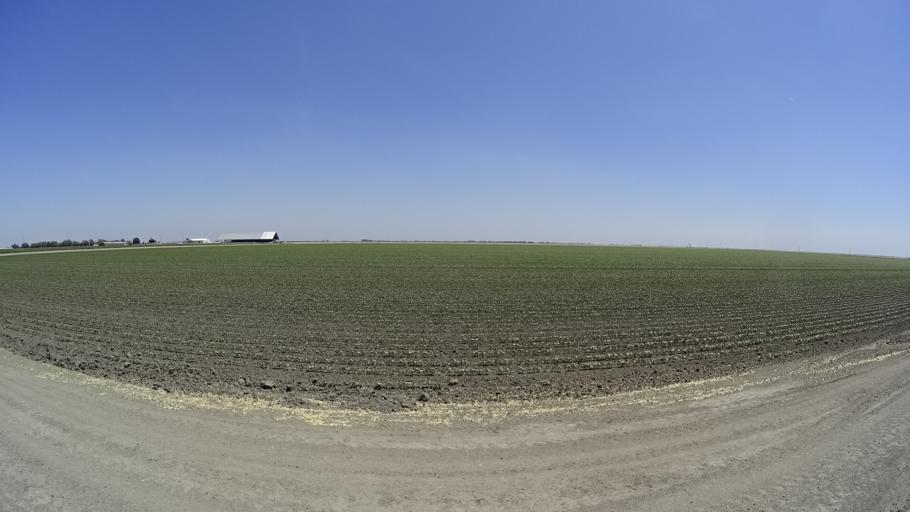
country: US
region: California
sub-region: Kings County
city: Corcoran
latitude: 36.1035
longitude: -119.6443
